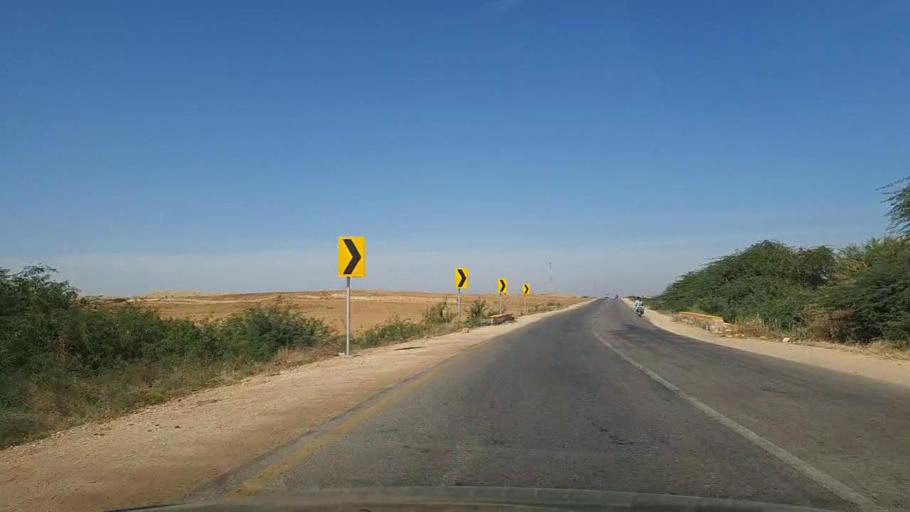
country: PK
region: Sindh
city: Kotri
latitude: 25.1918
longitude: 68.2387
